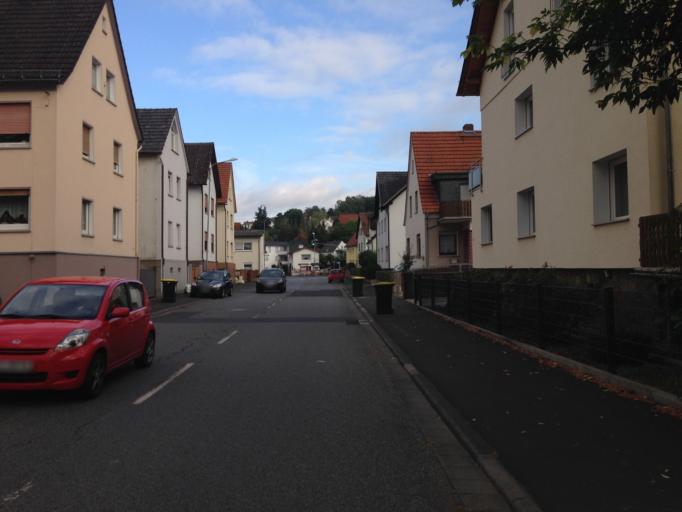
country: DE
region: Hesse
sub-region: Regierungsbezirk Giessen
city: Heuchelheim
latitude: 50.6246
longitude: 8.5843
